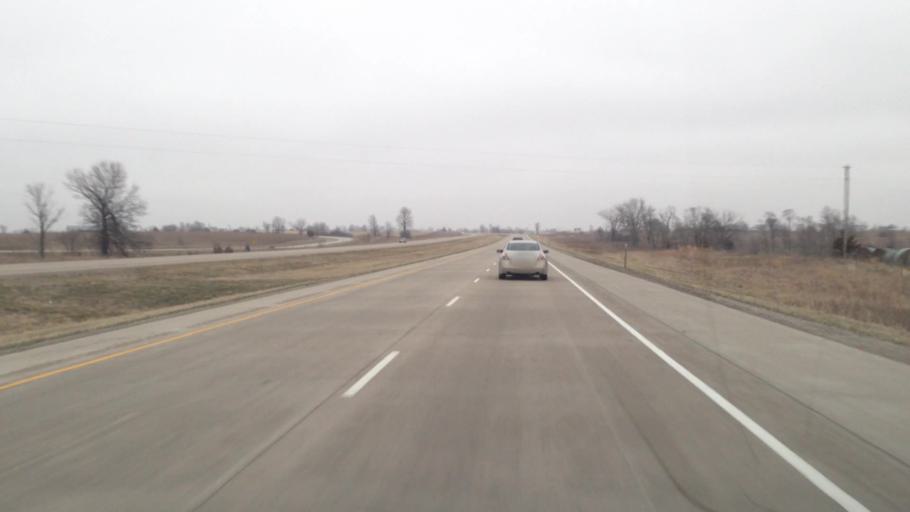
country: US
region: Iowa
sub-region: Decatur County
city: Leon
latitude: 40.8330
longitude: -93.8121
